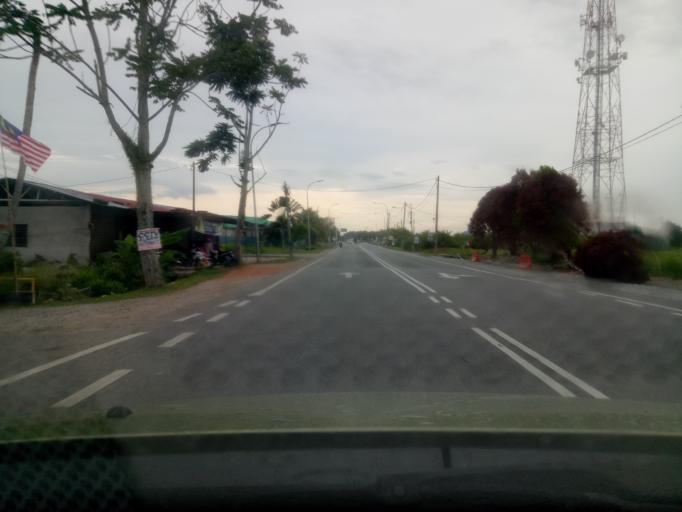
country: MY
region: Kedah
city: Gurun
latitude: 5.9775
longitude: 100.4500
